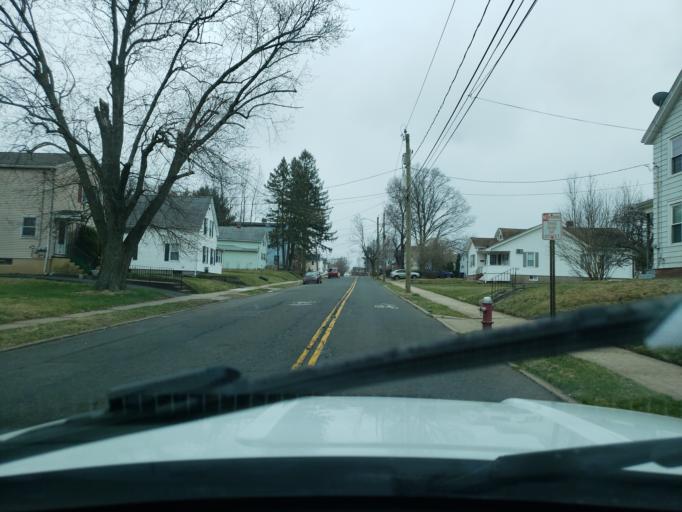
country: US
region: Connecticut
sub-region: Hartford County
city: New Britain
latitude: 41.6656
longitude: -72.7601
